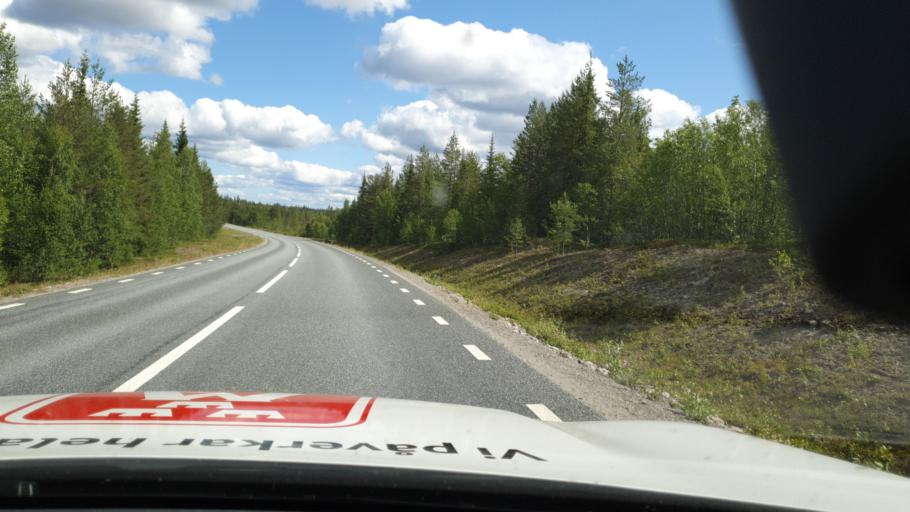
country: SE
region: Vaesterbotten
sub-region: Sorsele Kommun
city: Sorsele
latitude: 65.5578
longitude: 17.9233
